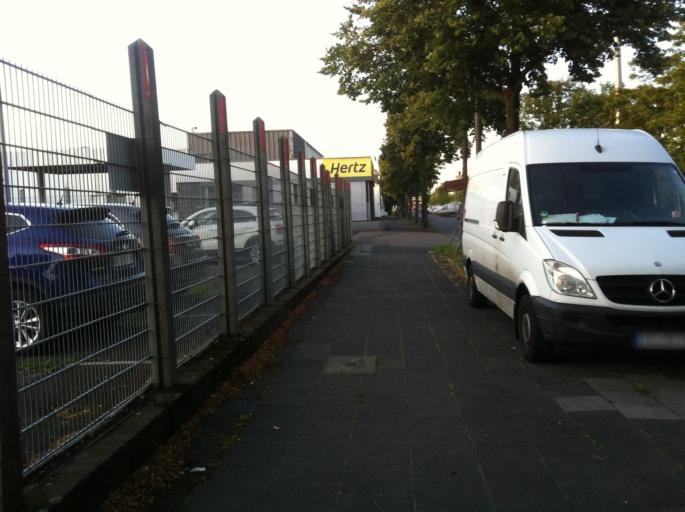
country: DE
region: North Rhine-Westphalia
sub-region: Regierungsbezirk Koln
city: Poll
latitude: 50.9009
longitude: 7.0196
